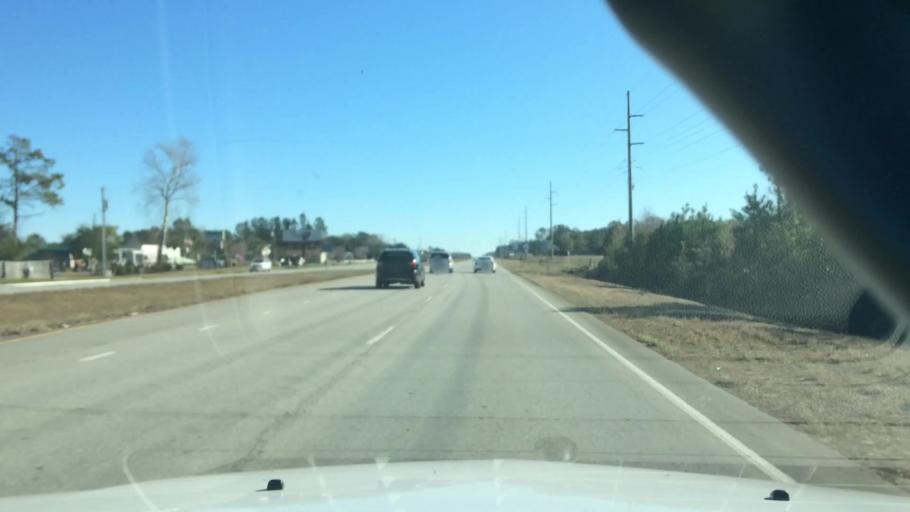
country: US
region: North Carolina
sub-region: Brunswick County
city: Sunset Beach
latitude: 33.9488
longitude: -78.4854
